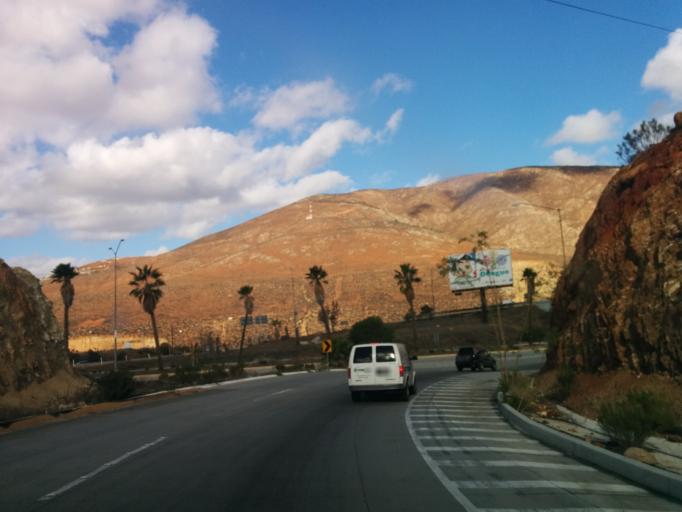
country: MX
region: Baja California
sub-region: Tijuana
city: Ejido Javier Rojo Gomez
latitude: 32.5409
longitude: -116.8543
